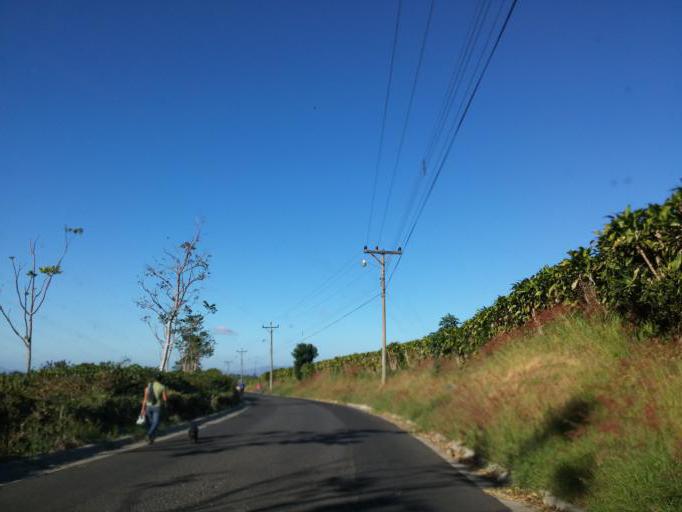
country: CR
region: Alajuela
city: Sabanilla
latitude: 10.0768
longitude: -84.1969
